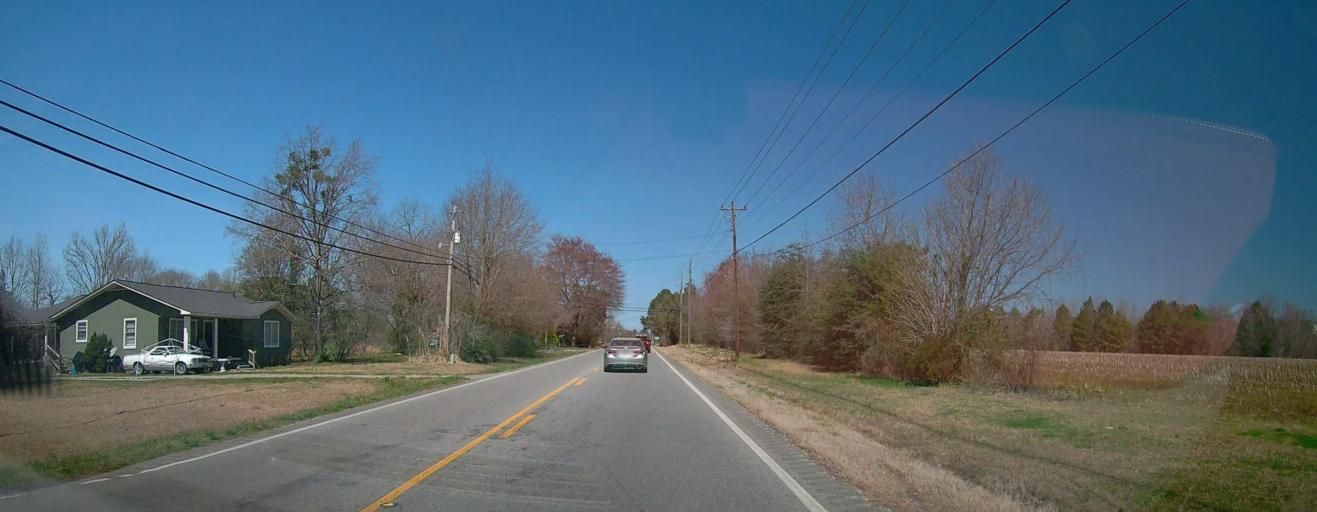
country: US
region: Alabama
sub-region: Etowah County
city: Southside
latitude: 33.8918
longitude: -86.0308
